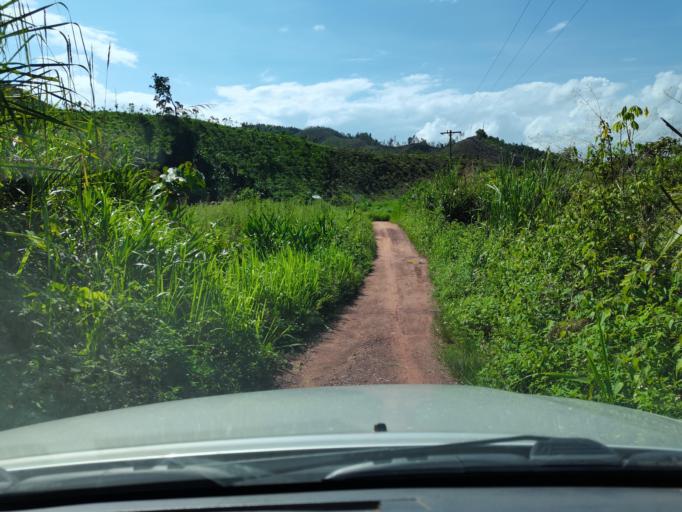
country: LA
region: Loungnamtha
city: Muang Nale
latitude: 20.5614
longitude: 101.0589
